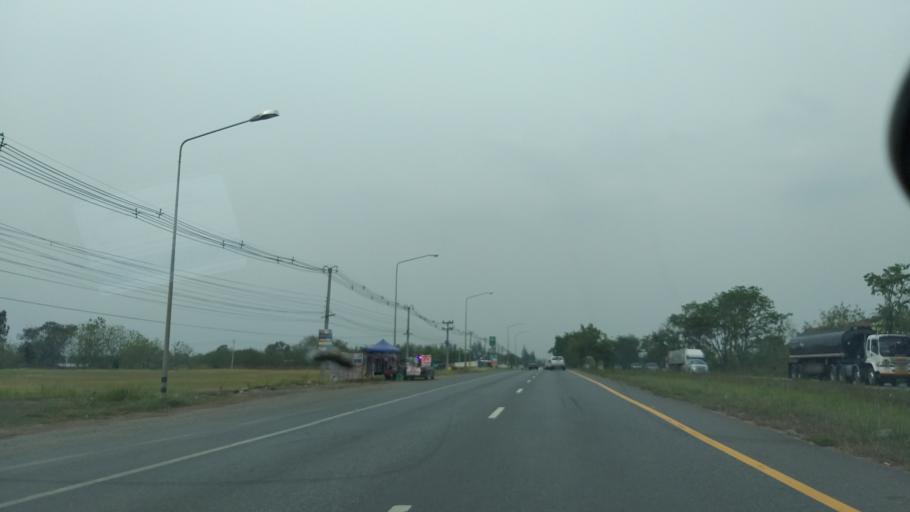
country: TH
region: Chon Buri
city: Ko Chan
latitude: 13.2948
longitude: 101.2599
